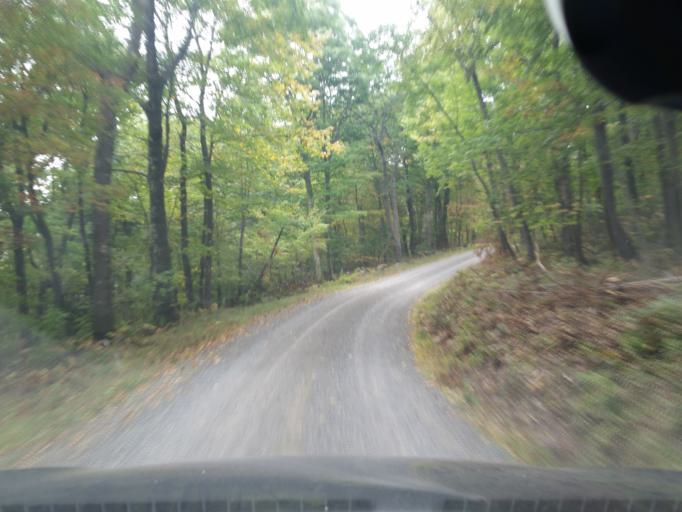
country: US
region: Pennsylvania
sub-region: Lycoming County
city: Jersey Shore
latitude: 41.0830
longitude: -77.2092
